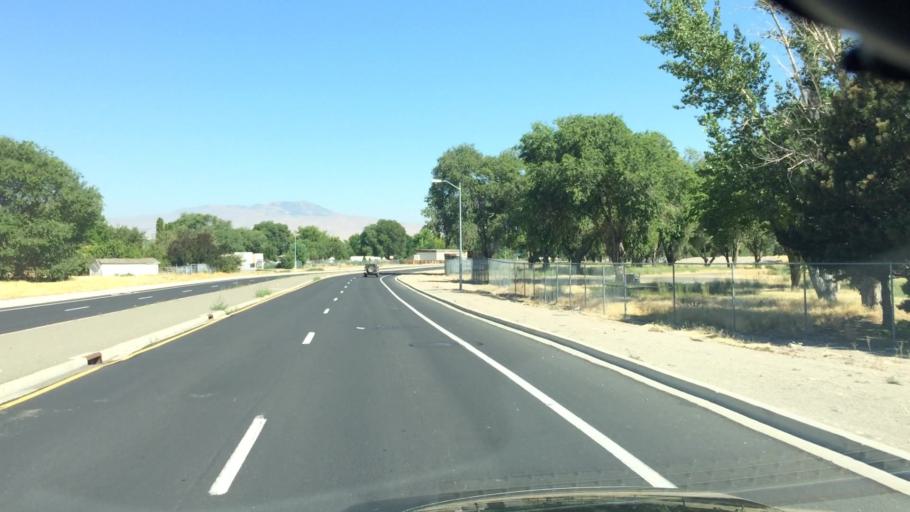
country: US
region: Nevada
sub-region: Washoe County
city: Sparks
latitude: 39.4835
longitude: -119.7737
